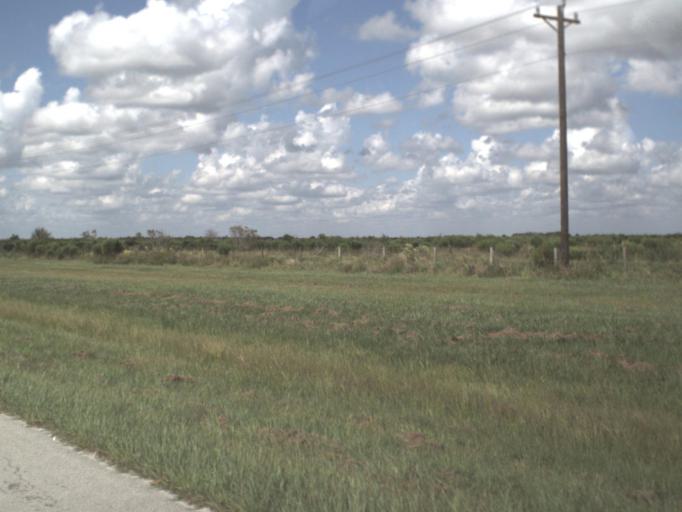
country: US
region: Florida
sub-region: Collier County
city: Immokalee
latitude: 26.4905
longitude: -81.4538
